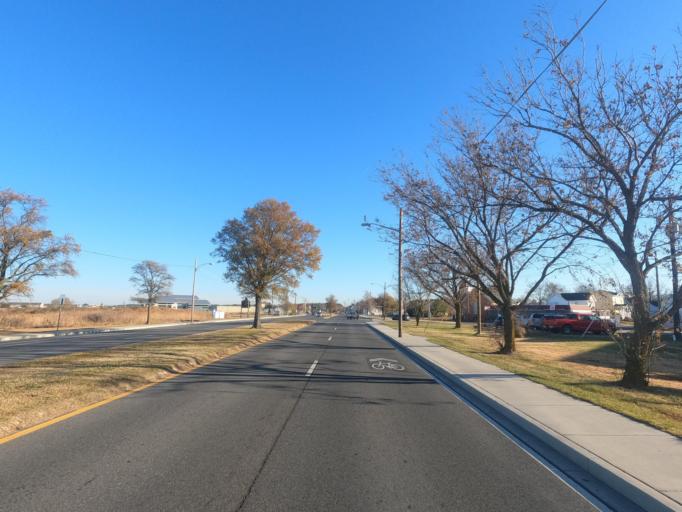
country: US
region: Maryland
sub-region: Somerset County
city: Crisfield
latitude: 37.9825
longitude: -75.8555
